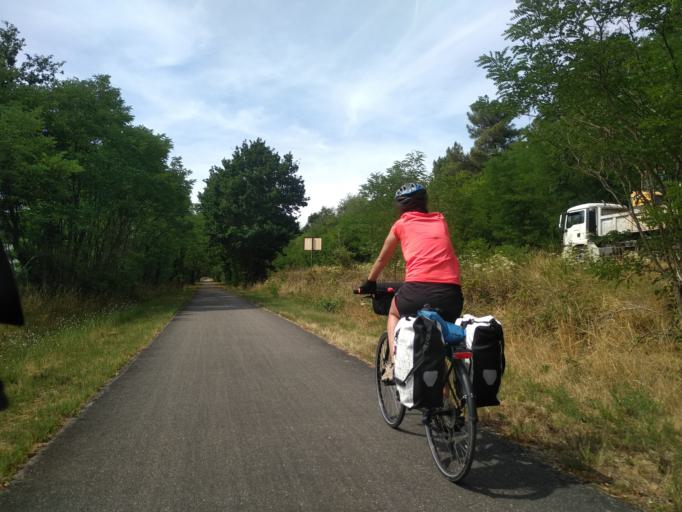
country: FR
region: Auvergne
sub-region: Departement de l'Allier
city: Diou
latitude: 46.5448
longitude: 3.7448
